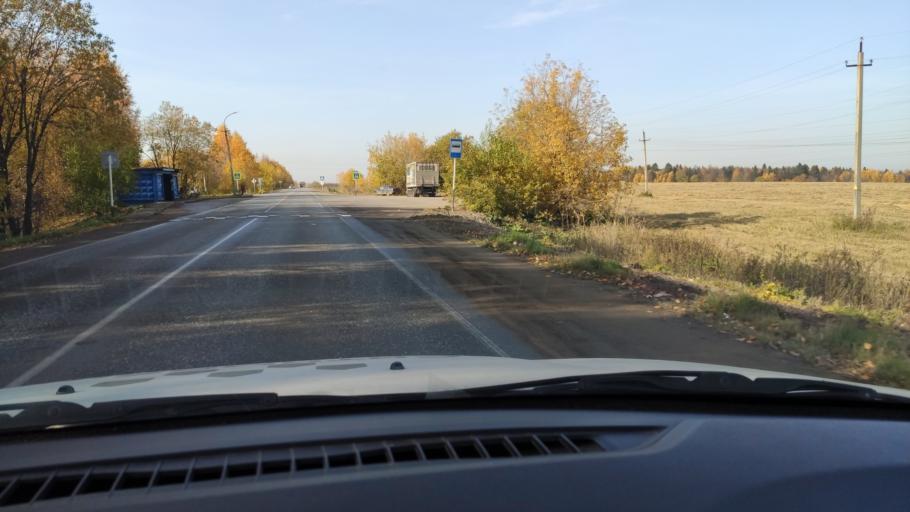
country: RU
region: Perm
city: Sylva
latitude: 58.0284
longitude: 56.7106
